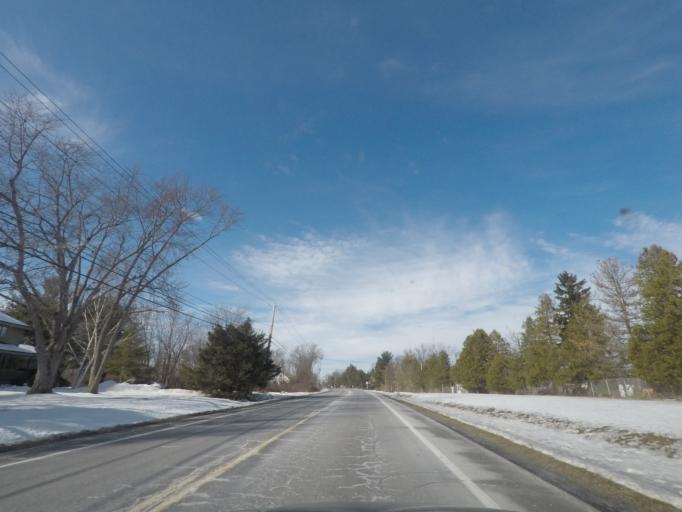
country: US
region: New York
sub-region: Albany County
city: Voorheesville
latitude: 42.6923
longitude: -73.9662
